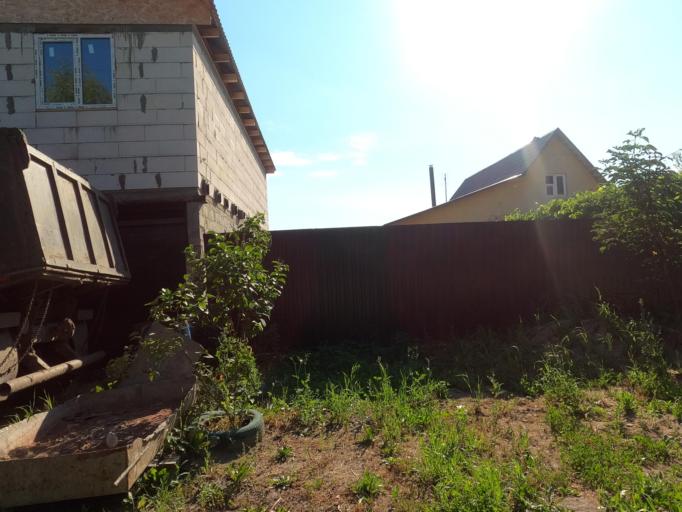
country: RU
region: Moskovskaya
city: Konobeyevo
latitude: 55.4094
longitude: 38.6998
